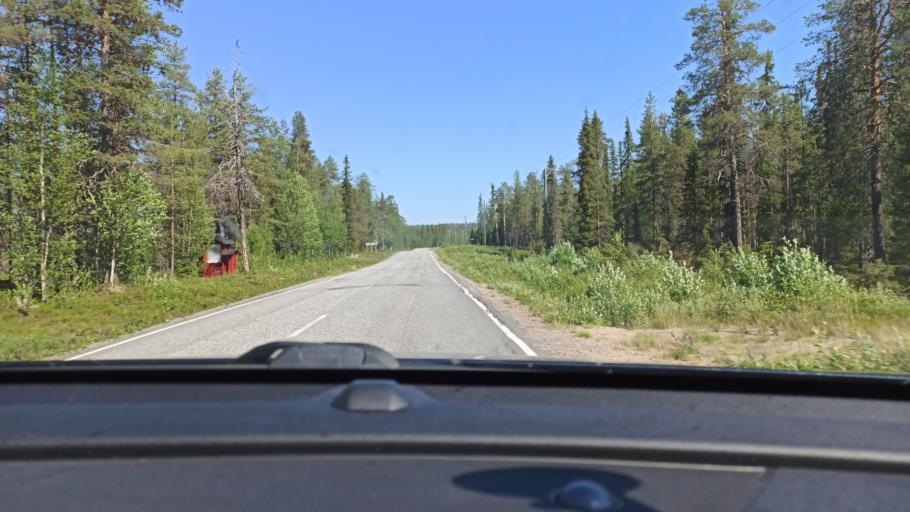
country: FI
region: Lapland
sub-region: Tunturi-Lappi
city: Kolari
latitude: 67.6268
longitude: 24.1556
